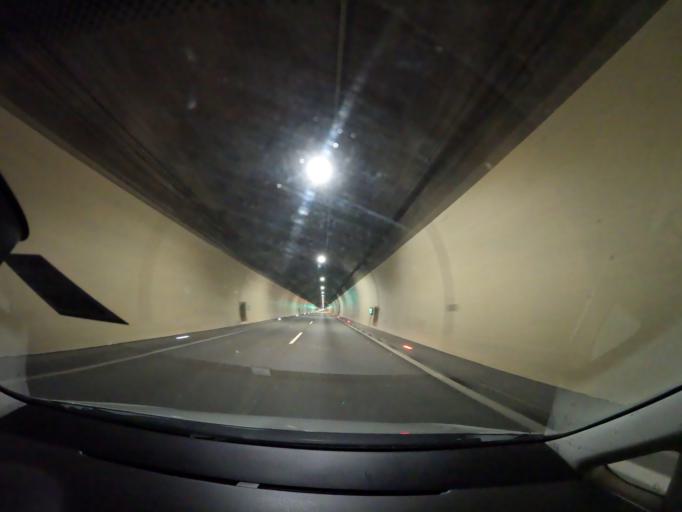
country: AT
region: Carinthia
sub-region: Politischer Bezirk Wolfsberg
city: Bad Sankt Leonhard im Lavanttal
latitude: 46.9070
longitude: 14.8227
